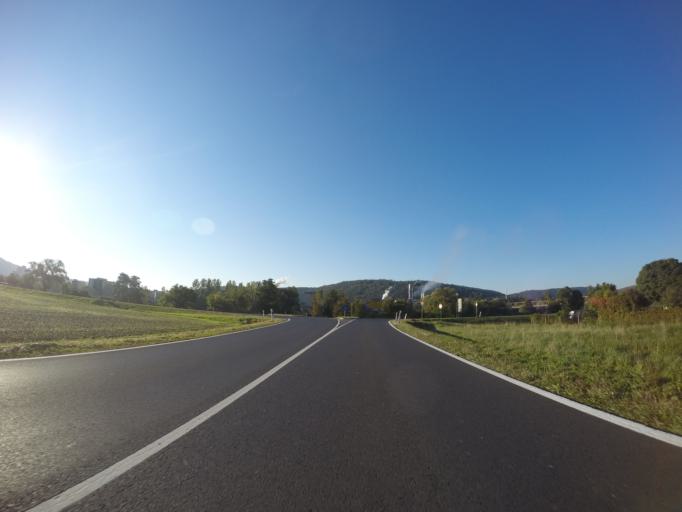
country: DE
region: Bavaria
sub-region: Regierungsbezirk Unterfranken
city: Hasloch
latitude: 49.7908
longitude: 9.4942
